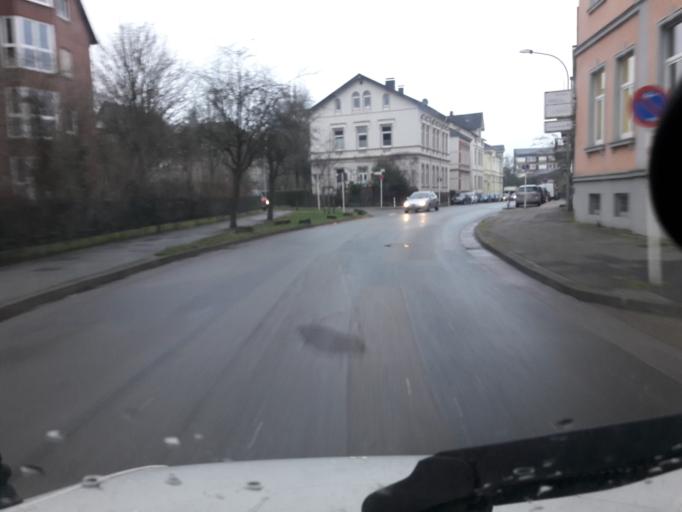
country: DE
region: North Rhine-Westphalia
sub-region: Regierungsbezirk Detmold
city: Minden
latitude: 52.2922
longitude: 8.9225
